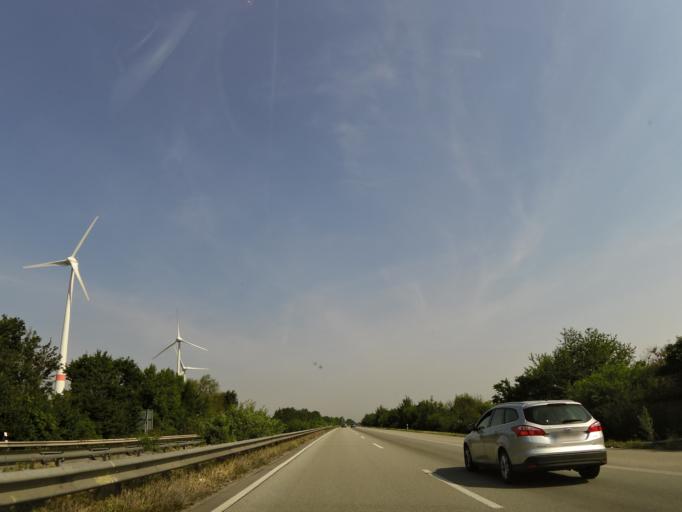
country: DE
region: Rheinland-Pfalz
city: Heuchelheim bei Frankenthal
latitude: 49.5820
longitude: 8.2939
